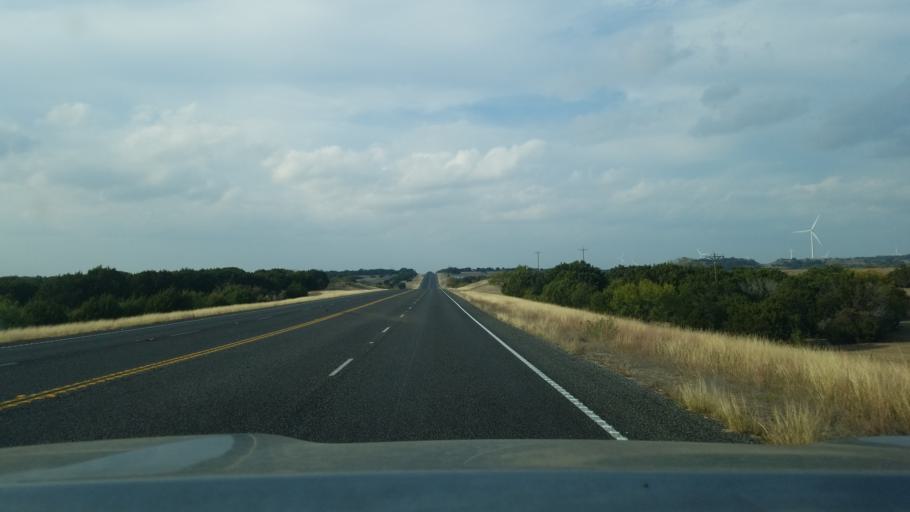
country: US
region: Texas
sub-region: Mills County
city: Goldthwaite
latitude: 31.3462
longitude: -98.5022
